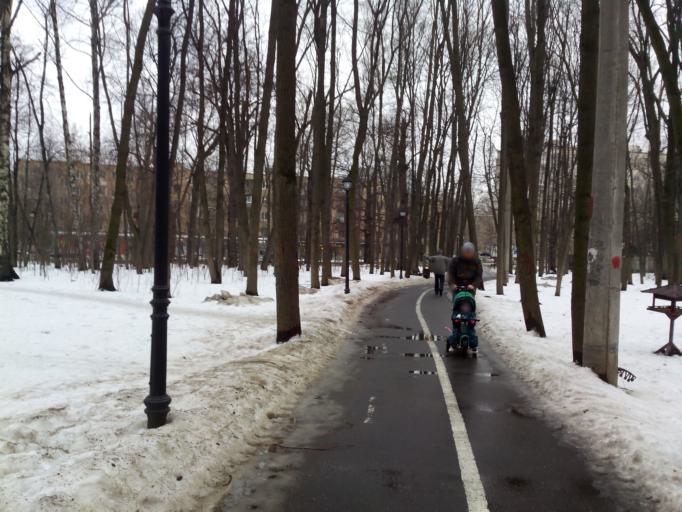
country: RU
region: Moskovskaya
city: Fili
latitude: 55.7427
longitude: 37.4752
